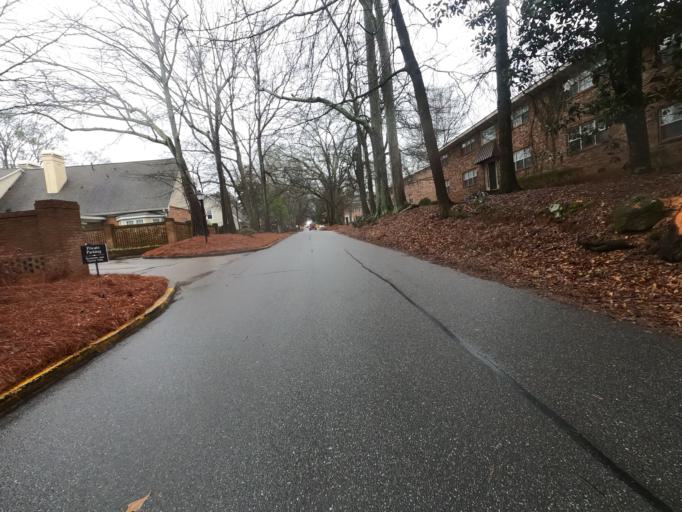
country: US
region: Georgia
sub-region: Clarke County
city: Athens
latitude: 33.9542
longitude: -83.3852
